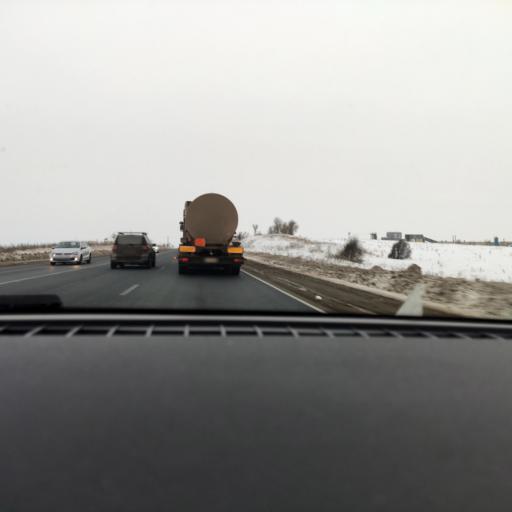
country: RU
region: Samara
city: Novosemeykino
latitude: 53.3869
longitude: 50.4293
